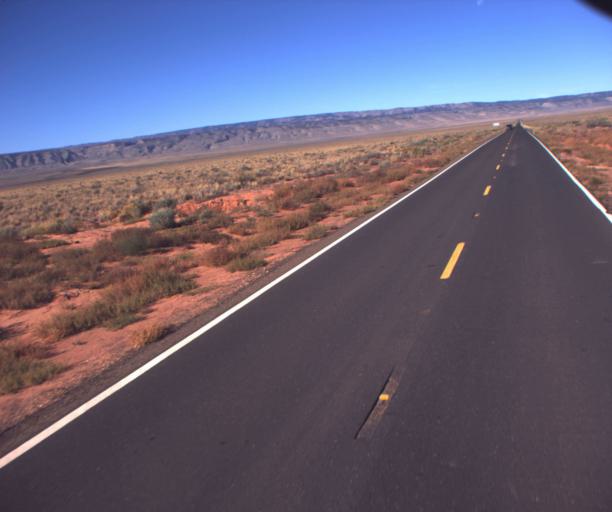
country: US
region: Arizona
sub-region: Coconino County
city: Page
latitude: 36.6958
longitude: -111.9078
